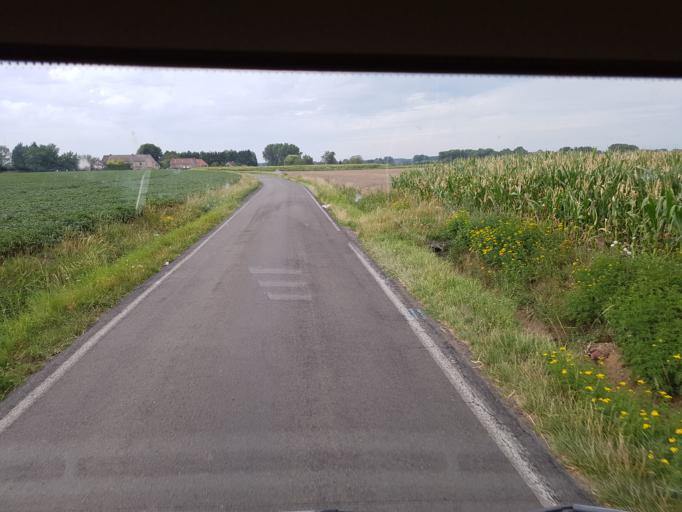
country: FR
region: Nord-Pas-de-Calais
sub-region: Departement du Nord
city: Vieux-Conde
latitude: 50.4886
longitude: 3.5546
